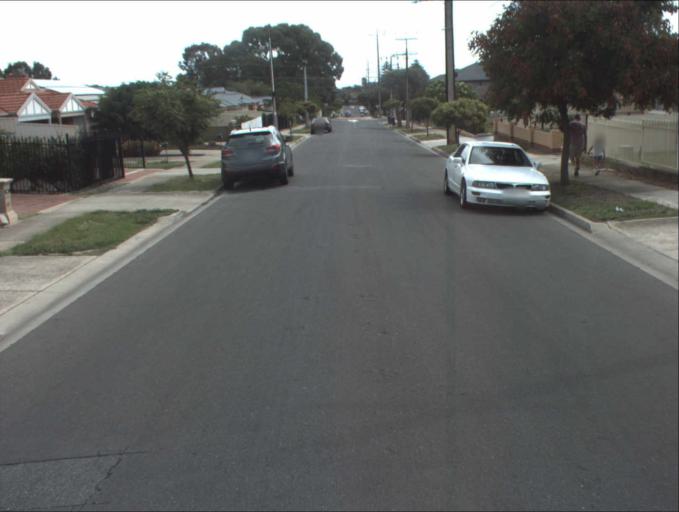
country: AU
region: South Australia
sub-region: Port Adelaide Enfield
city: Enfield
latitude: -34.8606
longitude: 138.6141
